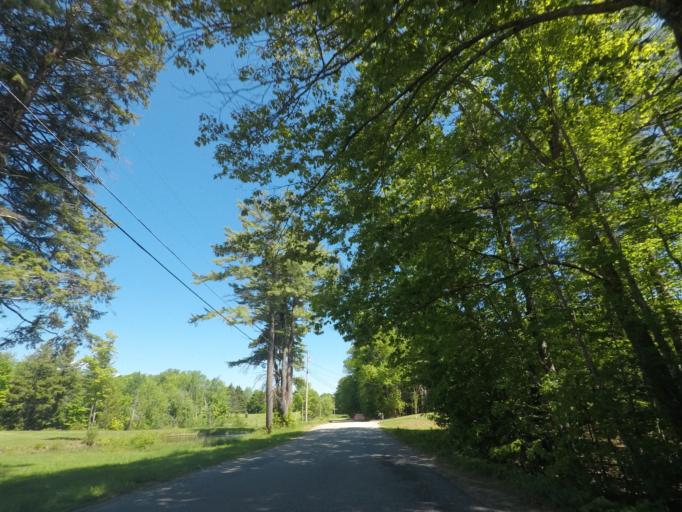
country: US
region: Maine
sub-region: Kennebec County
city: Winthrop
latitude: 44.2626
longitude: -69.9135
